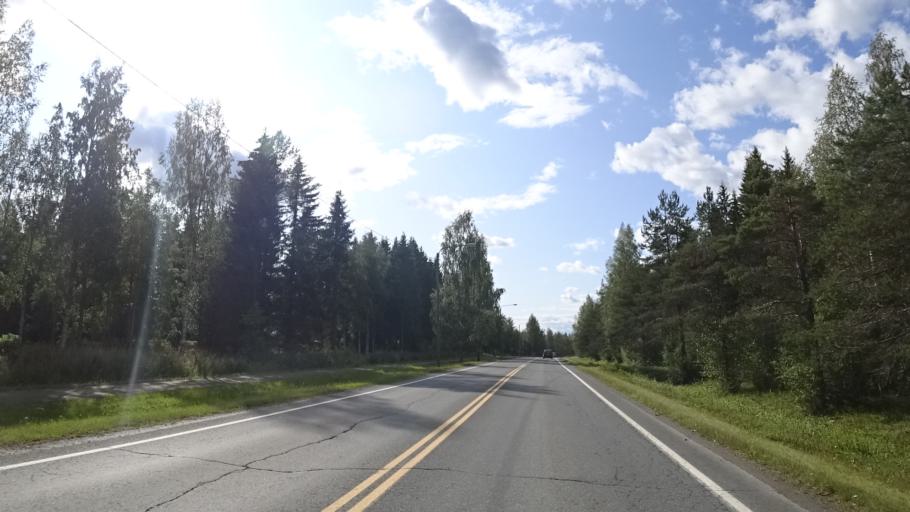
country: FI
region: North Karelia
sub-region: Keski-Karjala
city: Tohmajaervi
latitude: 62.2223
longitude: 30.3518
